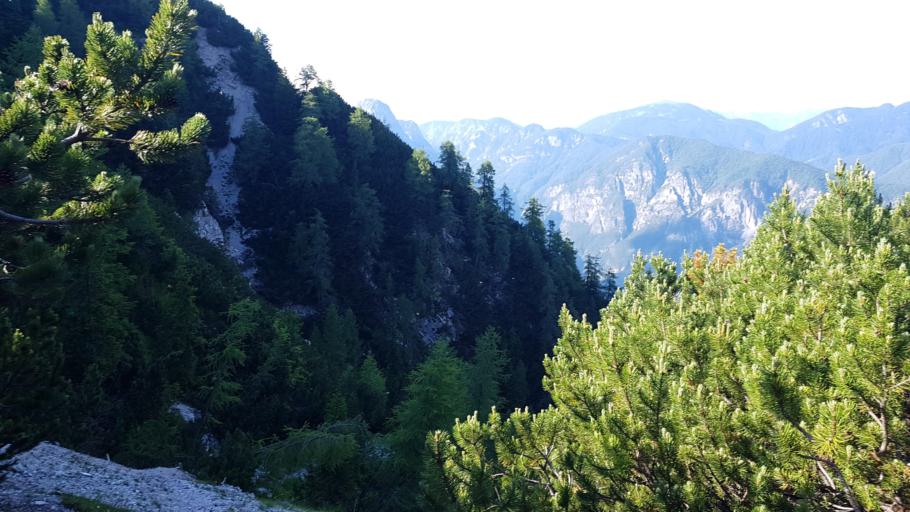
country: IT
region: Friuli Venezia Giulia
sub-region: Provincia di Udine
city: Malborghetto
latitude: 46.4770
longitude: 13.3923
